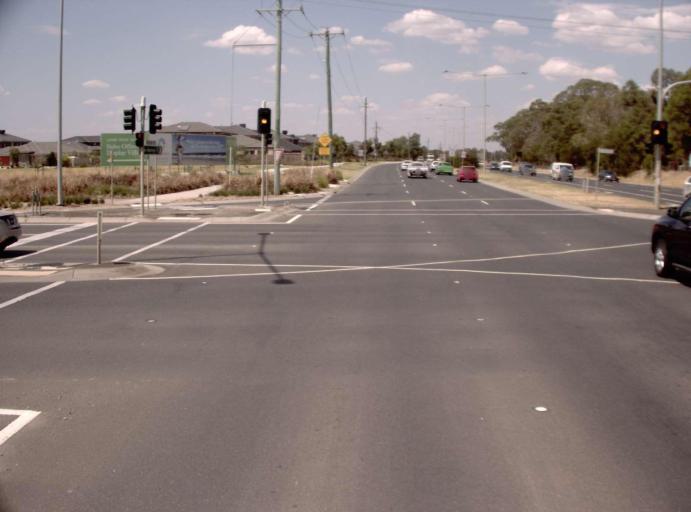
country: AU
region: Victoria
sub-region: Greater Dandenong
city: Keysborough
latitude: -38.0115
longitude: 145.1714
